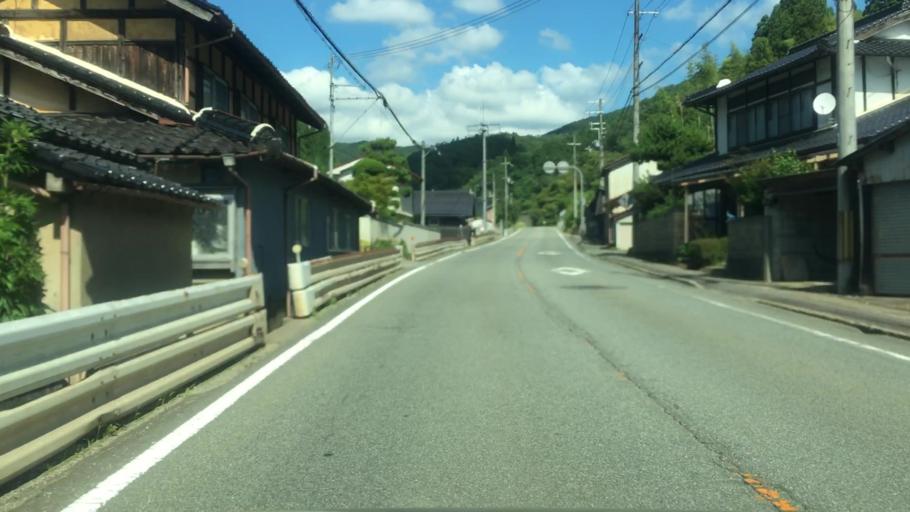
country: JP
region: Hyogo
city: Toyooka
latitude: 35.5742
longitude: 134.7662
